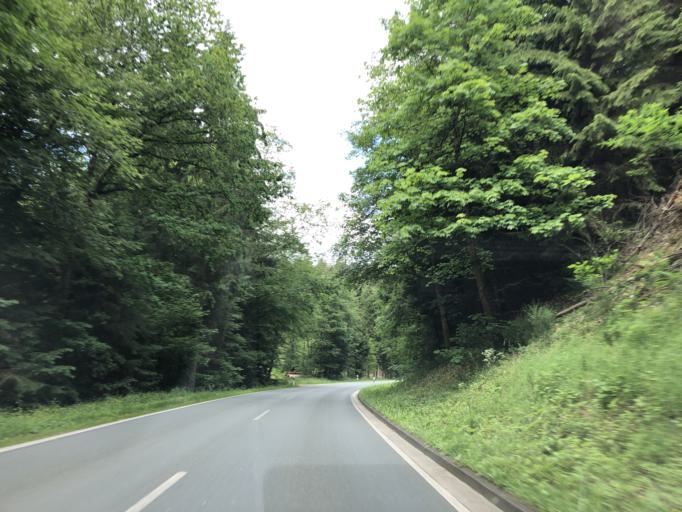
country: DE
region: North Rhine-Westphalia
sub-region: Regierungsbezirk Arnsberg
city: Kirchhundem
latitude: 51.0909
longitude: 8.1225
